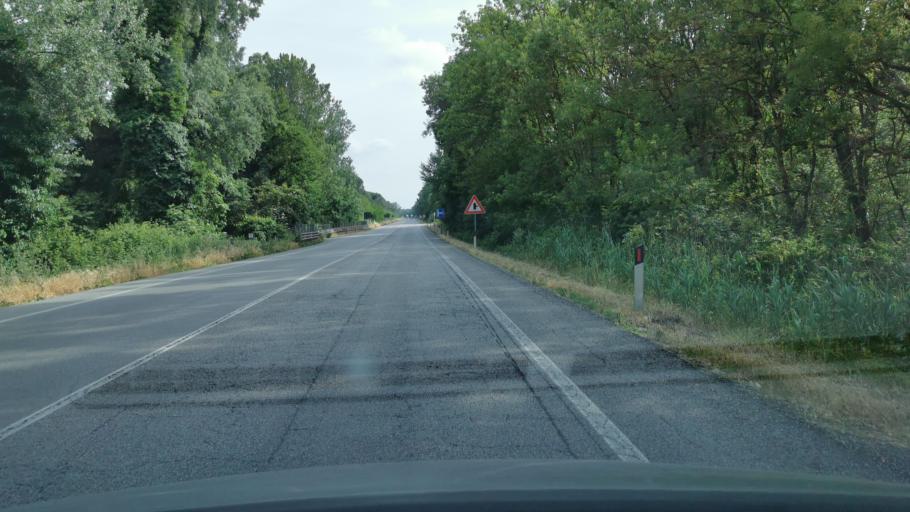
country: IT
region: Emilia-Romagna
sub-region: Provincia di Ravenna
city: Marina Romea
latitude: 44.5075
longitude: 12.2226
